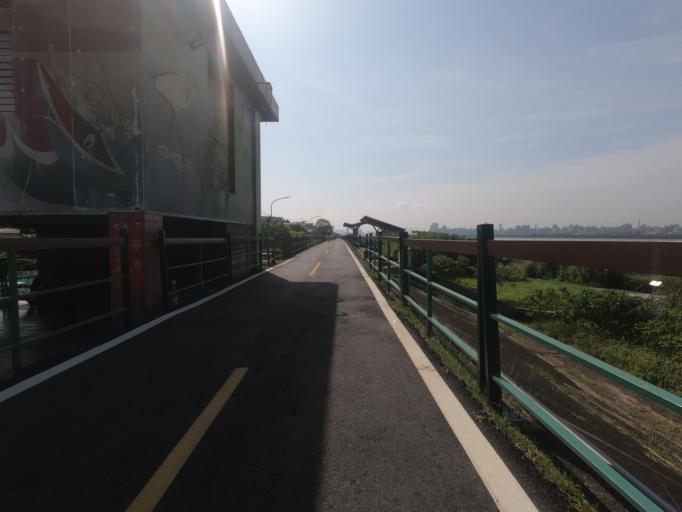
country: TW
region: Taipei
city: Taipei
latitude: 25.1071
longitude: 121.4704
